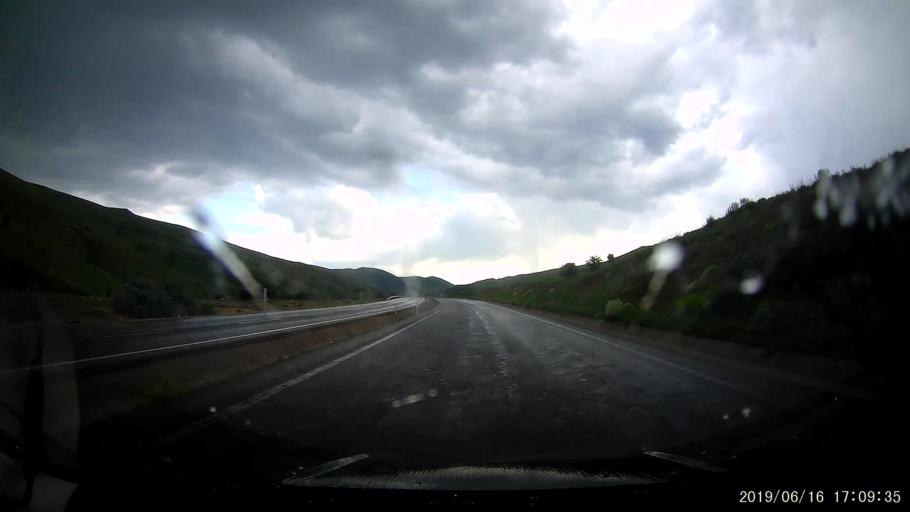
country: TR
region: Erzurum
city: Askale
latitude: 39.8929
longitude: 40.6484
